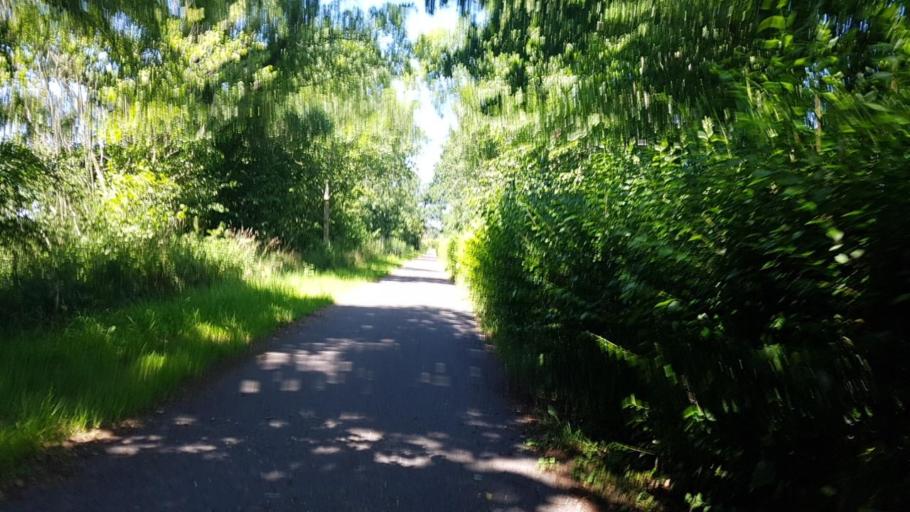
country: BE
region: Wallonia
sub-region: Province du Hainaut
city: Beaumont
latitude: 50.1760
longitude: 4.2319
